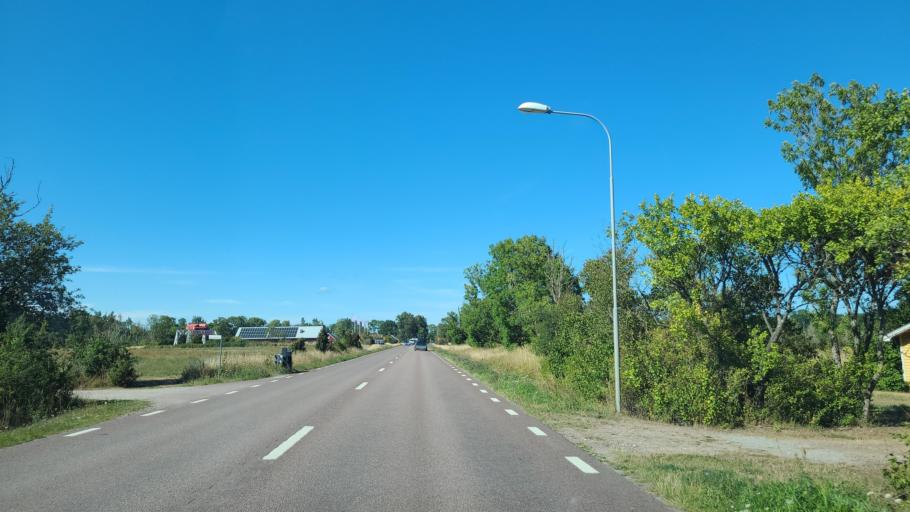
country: SE
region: Kalmar
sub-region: Borgholms Kommun
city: Borgholm
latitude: 57.1552
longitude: 17.0097
